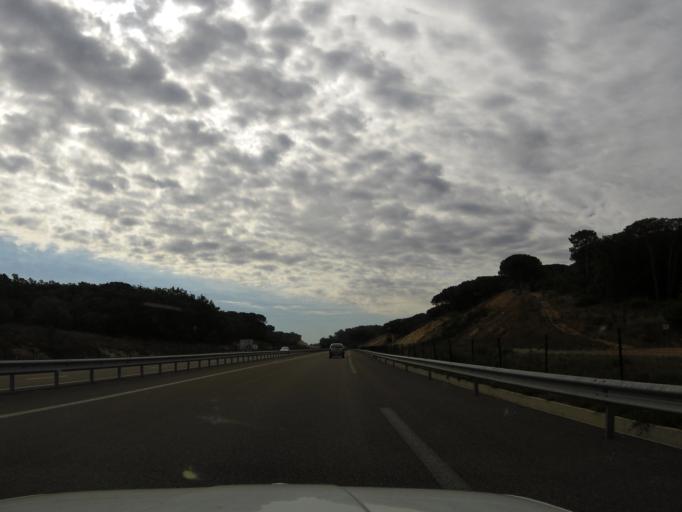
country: FR
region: Languedoc-Roussillon
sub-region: Departement du Gard
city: La Calmette
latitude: 43.9163
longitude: 4.2624
